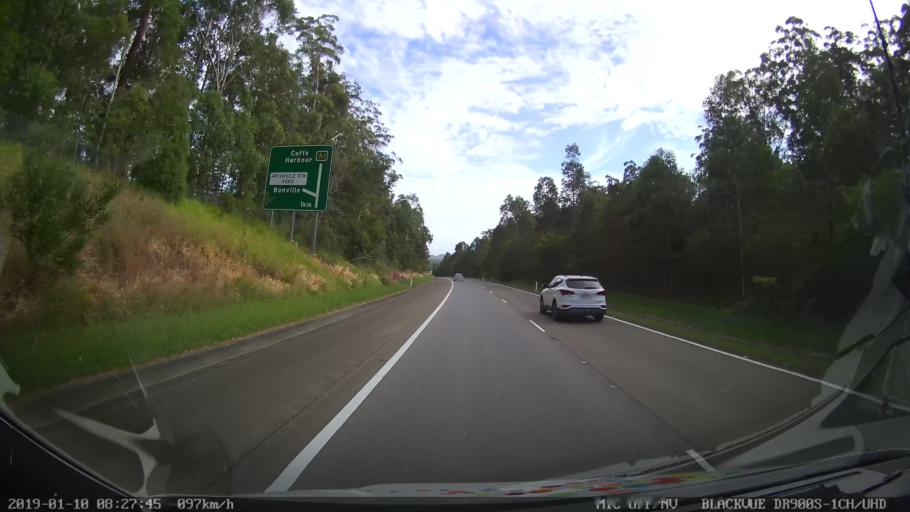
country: AU
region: New South Wales
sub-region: Coffs Harbour
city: Bonville
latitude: -30.4032
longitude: 153.0305
